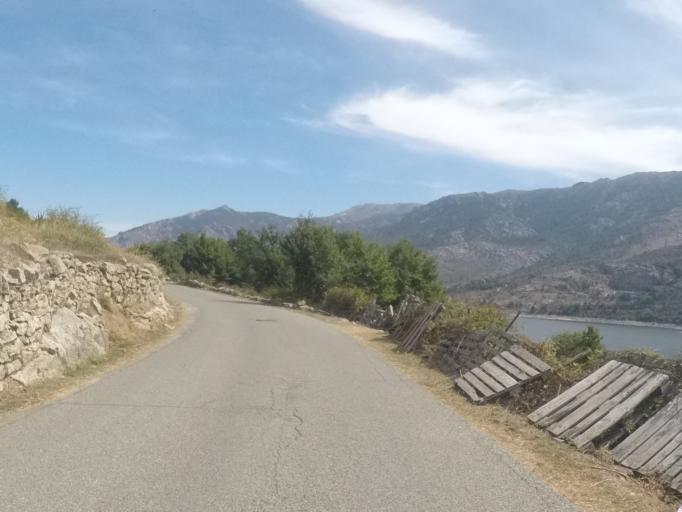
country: FR
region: Corsica
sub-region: Departement de la Haute-Corse
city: Corte
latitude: 42.3289
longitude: 9.0083
